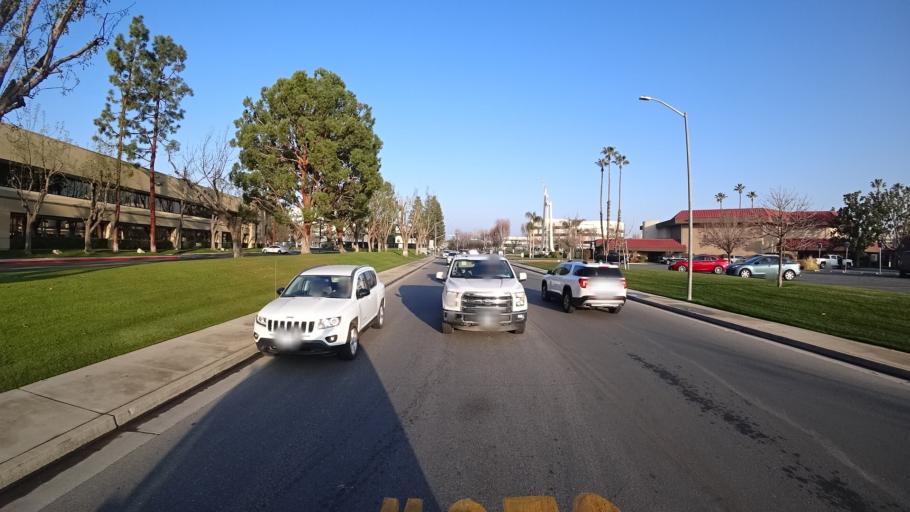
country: US
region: California
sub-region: Kern County
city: Bakersfield
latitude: 35.3630
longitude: -119.0563
